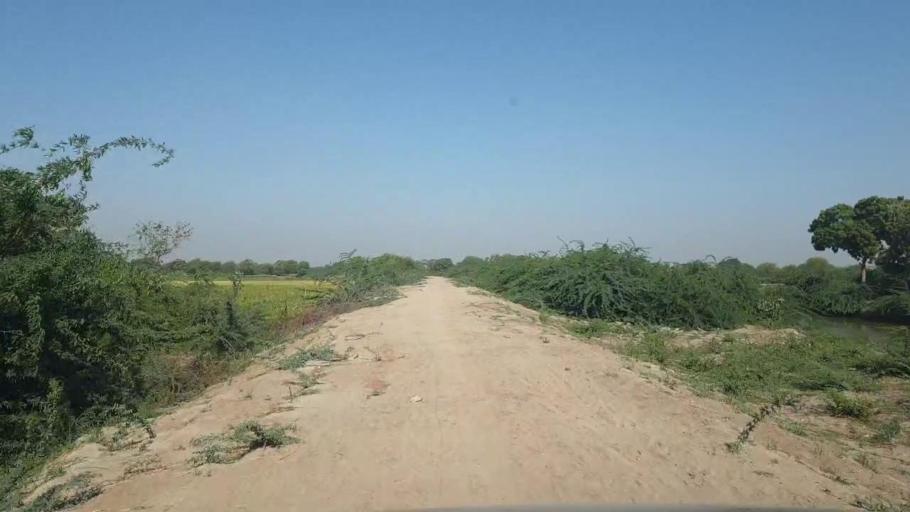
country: PK
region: Sindh
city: Talhar
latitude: 24.7873
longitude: 68.8081
